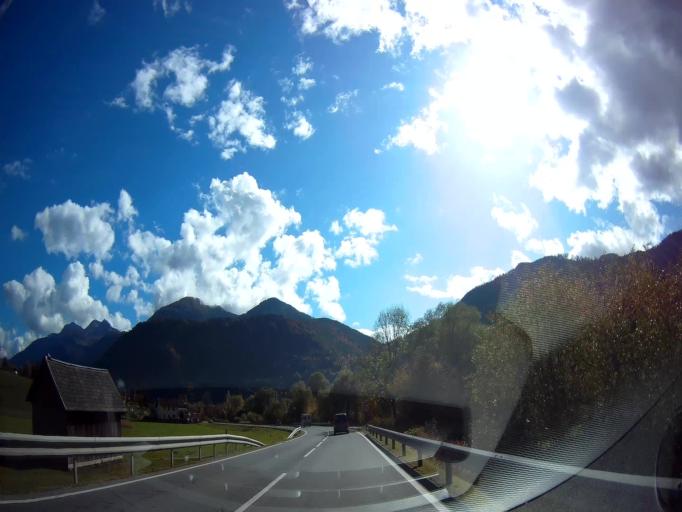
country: AT
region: Carinthia
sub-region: Politischer Bezirk Spittal an der Drau
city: Oberdrauburg
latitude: 46.7515
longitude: 12.9611
